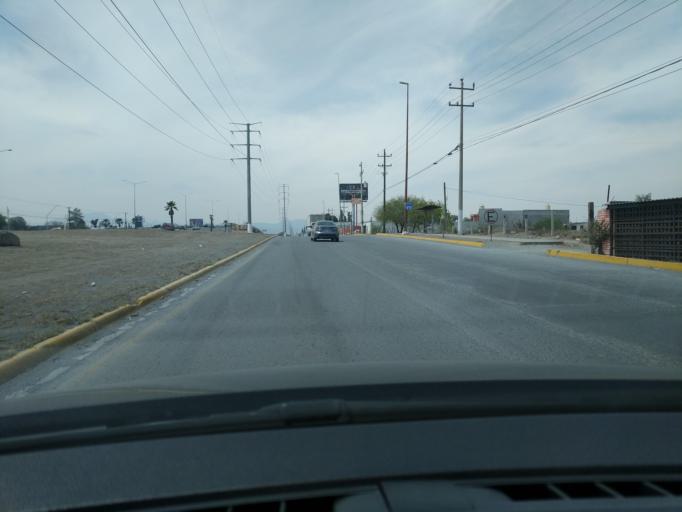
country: MX
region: Coahuila
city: Saltillo
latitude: 25.4313
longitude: -100.9436
